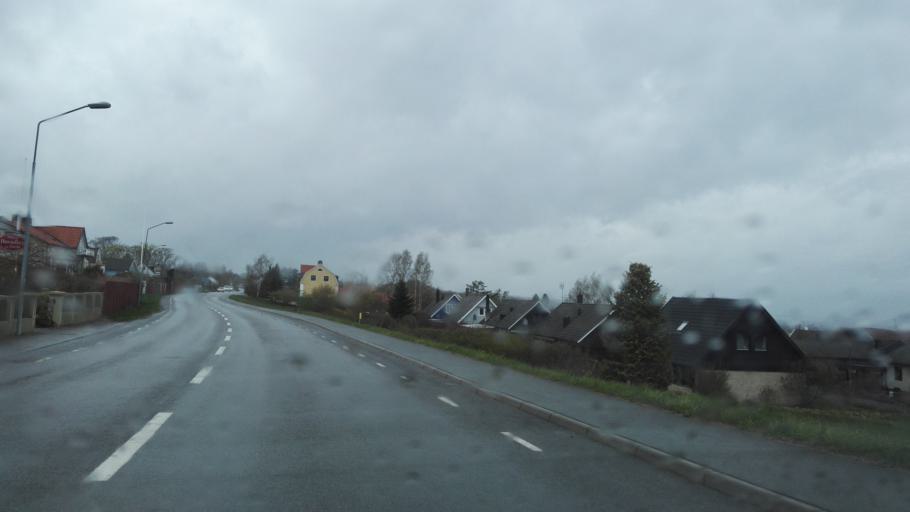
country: SE
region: Skane
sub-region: Simrishamns Kommun
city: Kivik
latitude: 55.6802
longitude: 14.2299
